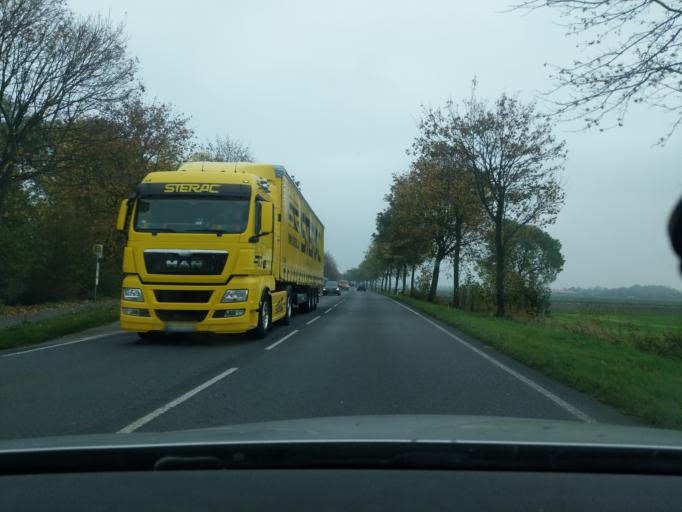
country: DE
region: Lower Saxony
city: Cuxhaven
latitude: 53.8322
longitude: 8.7415
